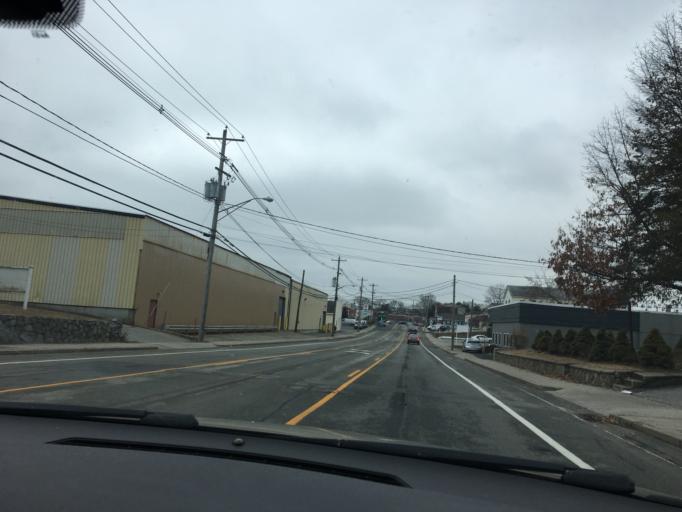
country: US
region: Rhode Island
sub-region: Providence County
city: Cranston
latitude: 41.7514
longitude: -71.4232
